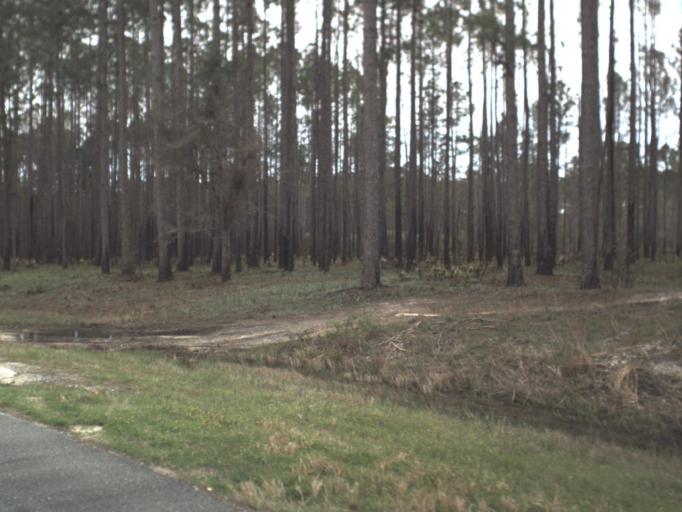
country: US
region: Florida
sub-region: Gadsden County
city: Midway
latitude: 30.3509
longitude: -84.5139
